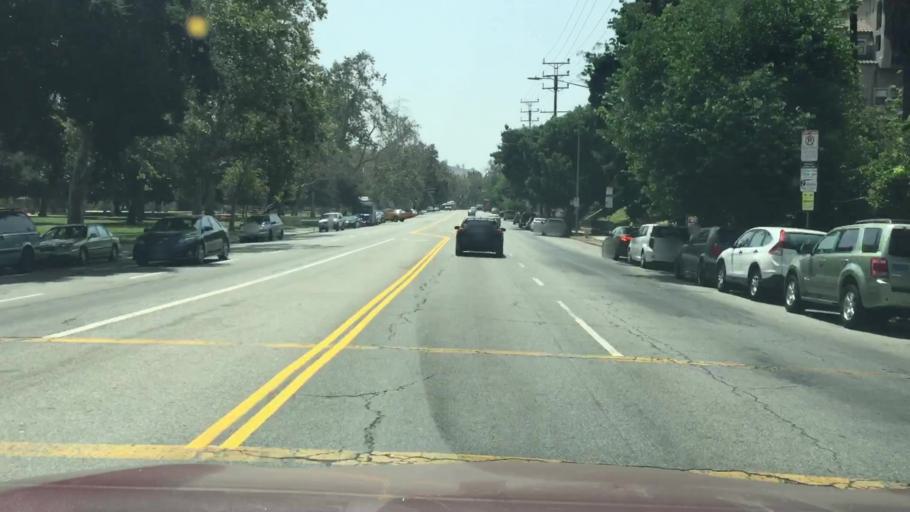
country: US
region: California
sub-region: Los Angeles County
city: South Pasadena
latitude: 34.1017
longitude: -118.2033
